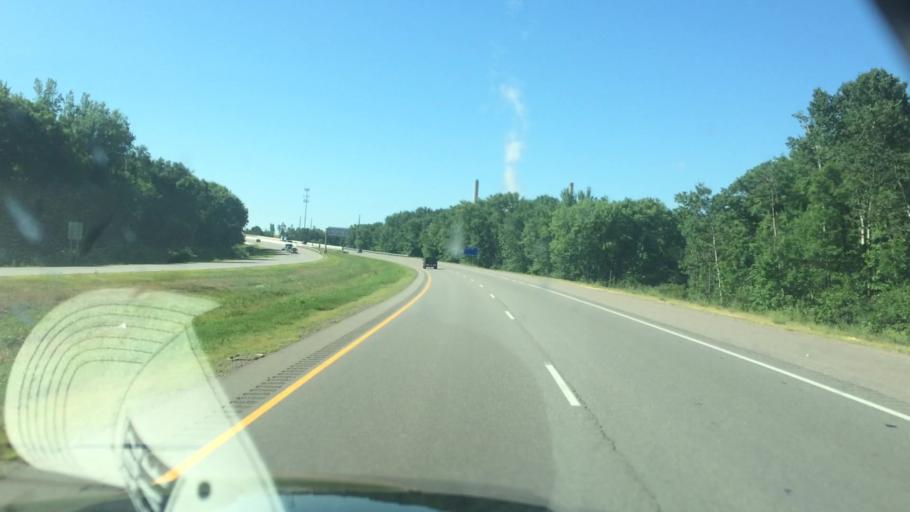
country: US
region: Wisconsin
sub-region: Marathon County
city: Rothschild
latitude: 44.8723
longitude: -89.6456
